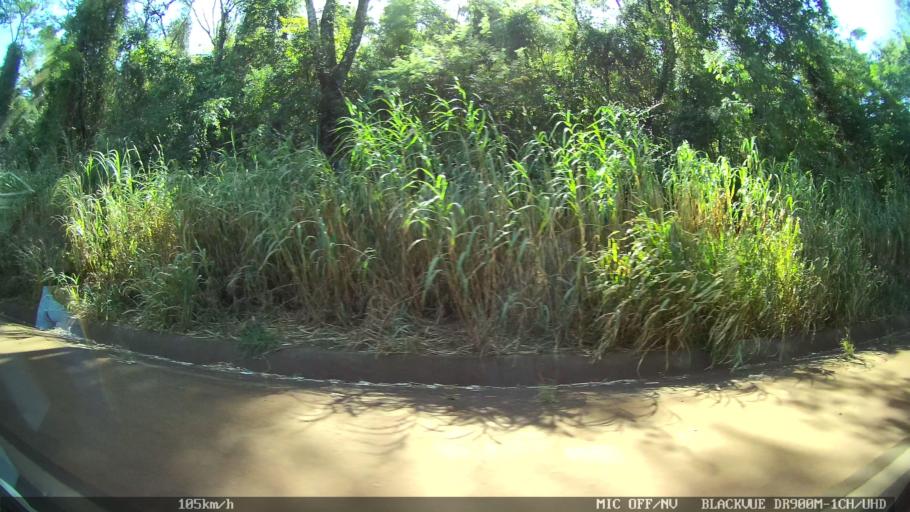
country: BR
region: Sao Paulo
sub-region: Sao Joaquim Da Barra
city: Sao Joaquim da Barra
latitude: -20.5534
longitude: -47.6677
